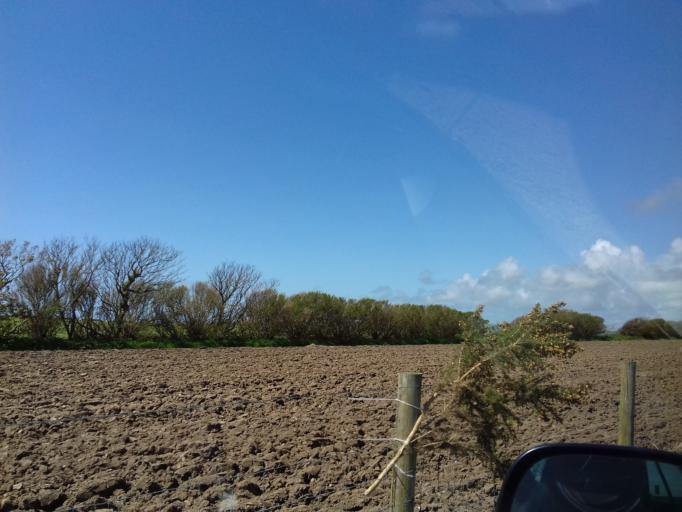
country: IE
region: Munster
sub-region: Waterford
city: Dunmore East
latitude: 52.1466
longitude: -6.9082
